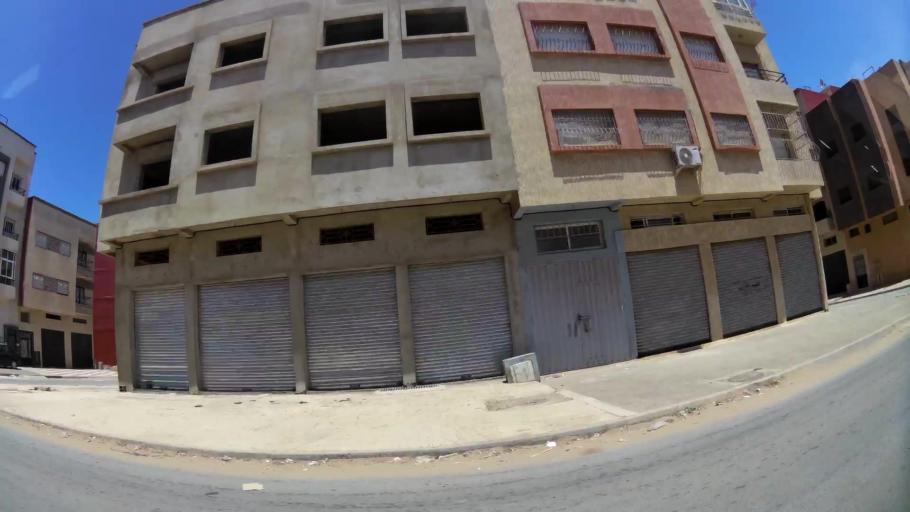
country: MA
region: Gharb-Chrarda-Beni Hssen
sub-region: Kenitra Province
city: Kenitra
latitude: 34.2322
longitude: -6.6136
